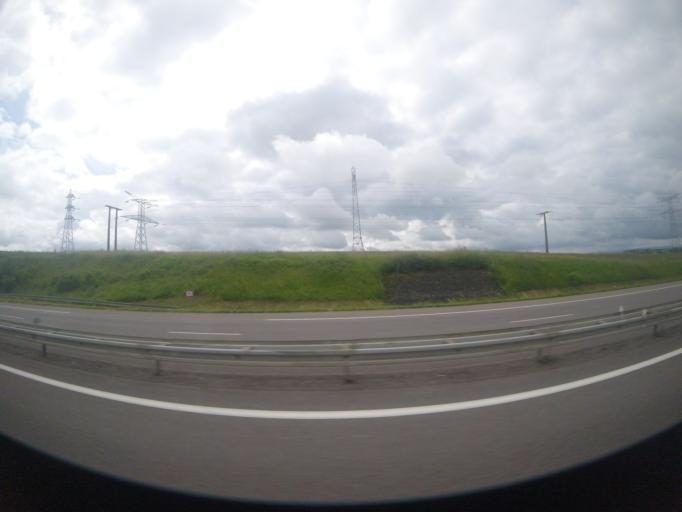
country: FR
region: Lorraine
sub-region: Departement de la Moselle
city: Saint-Privat-la-Montagne
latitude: 49.1814
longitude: 6.0264
